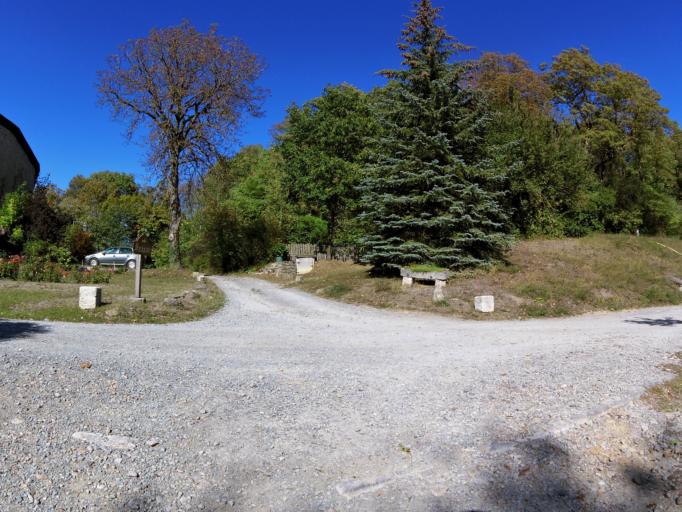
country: DE
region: Bavaria
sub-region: Regierungsbezirk Unterfranken
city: Reichenberg
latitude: 49.7314
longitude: 9.9198
